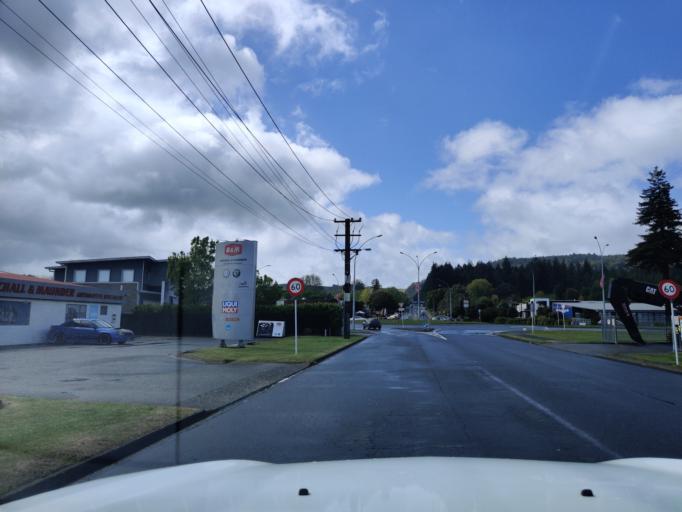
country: NZ
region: Bay of Plenty
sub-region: Rotorua District
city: Rotorua
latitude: -38.1473
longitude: 176.2758
